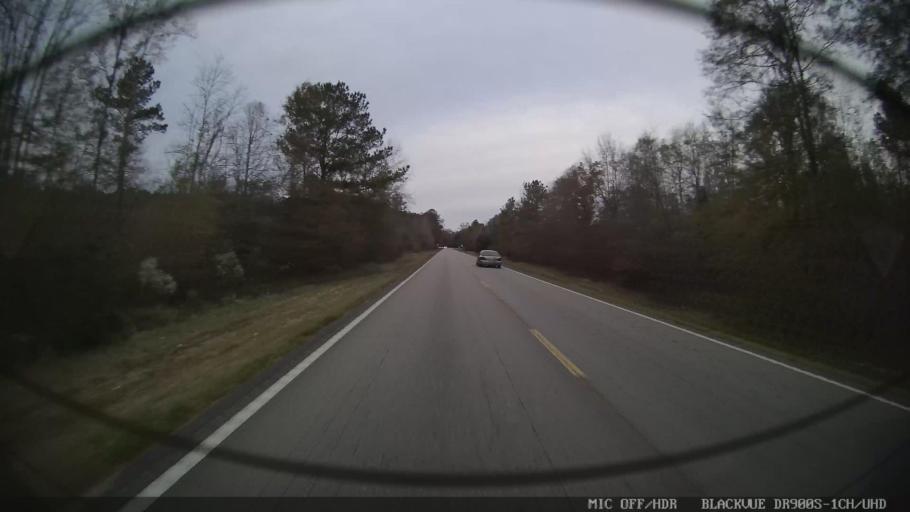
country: US
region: Mississippi
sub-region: Clarke County
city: Stonewall
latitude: 32.0365
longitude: -88.8762
